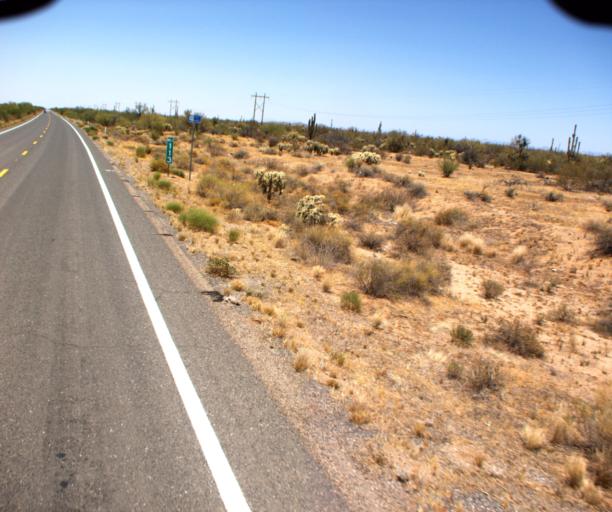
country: US
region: Arizona
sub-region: Pinal County
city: Florence
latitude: 32.7926
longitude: -111.1753
